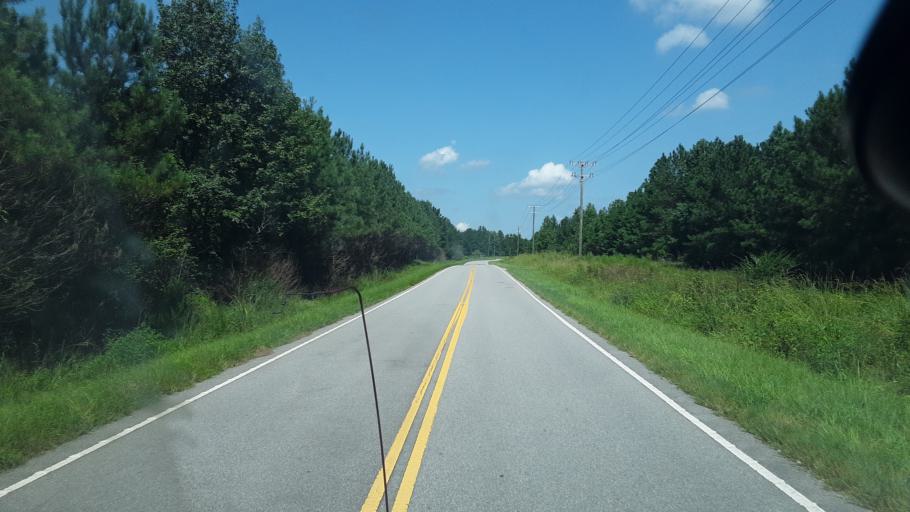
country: US
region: South Carolina
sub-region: Bamberg County
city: Bamberg
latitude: 33.4126
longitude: -81.0173
